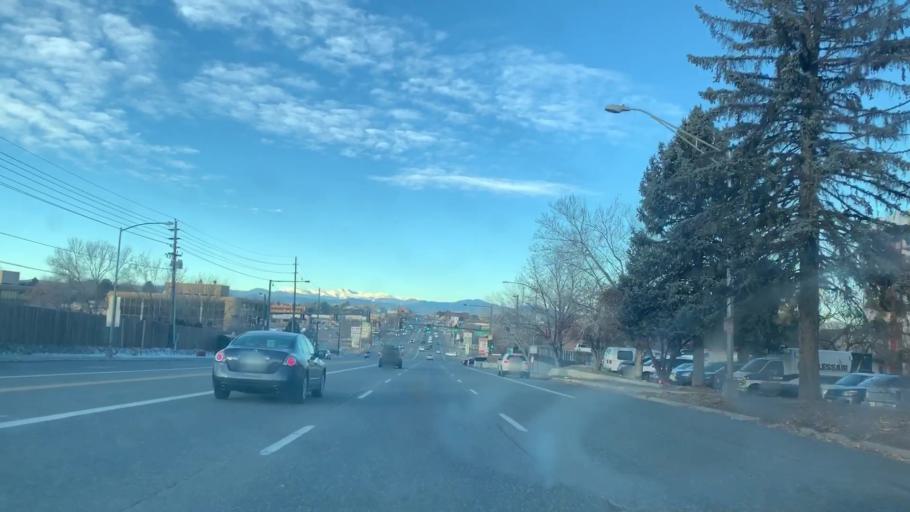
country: US
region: Colorado
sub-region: Arapahoe County
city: Cherry Hills Village
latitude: 39.6532
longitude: -104.8974
